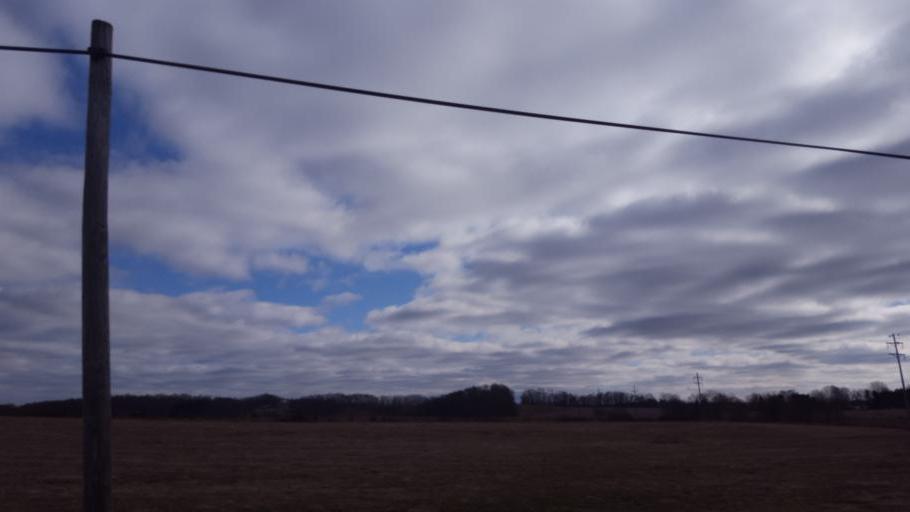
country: US
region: Ohio
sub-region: Knox County
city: Fredericktown
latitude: 40.5264
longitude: -82.5040
